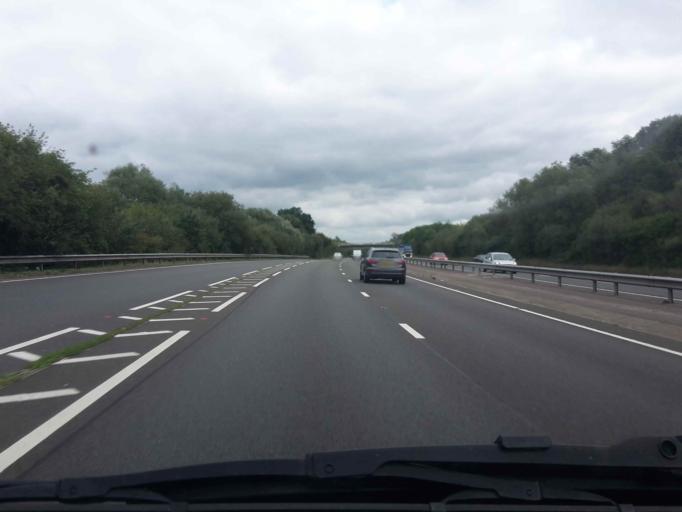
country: GB
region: England
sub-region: Surrey
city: Seale
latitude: 51.2451
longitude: -0.7353
